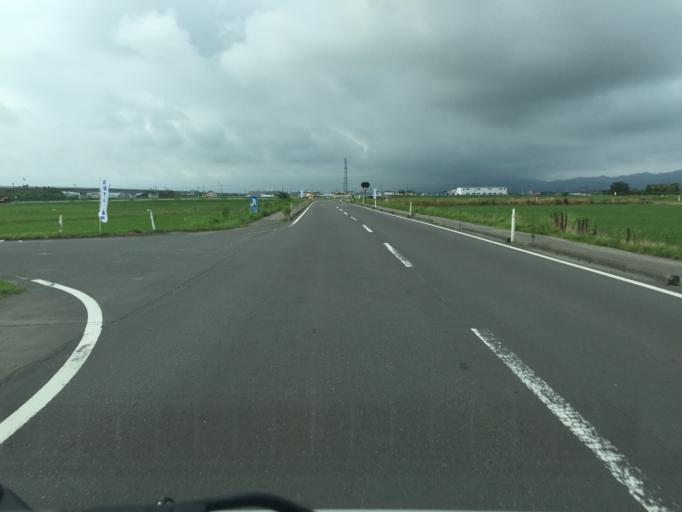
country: JP
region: Miyagi
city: Watari
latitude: 38.0390
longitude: 140.8897
